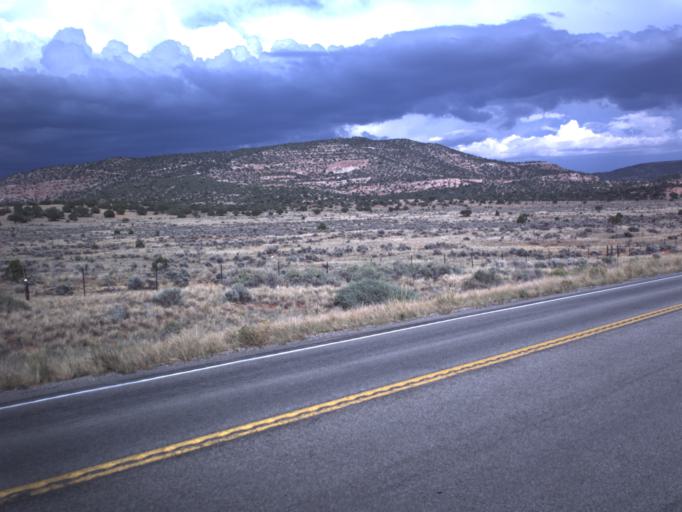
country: US
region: Utah
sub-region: Grand County
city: Moab
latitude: 38.3173
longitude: -109.4161
